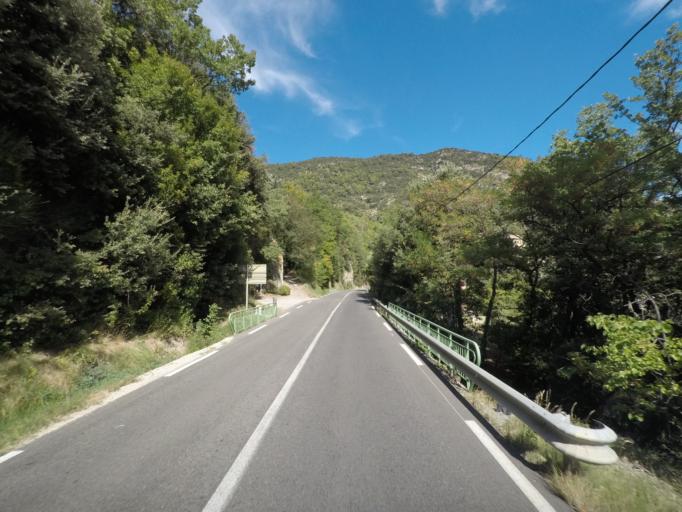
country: FR
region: Rhone-Alpes
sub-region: Departement de la Drome
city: Nyons
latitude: 44.3694
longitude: 5.1509
